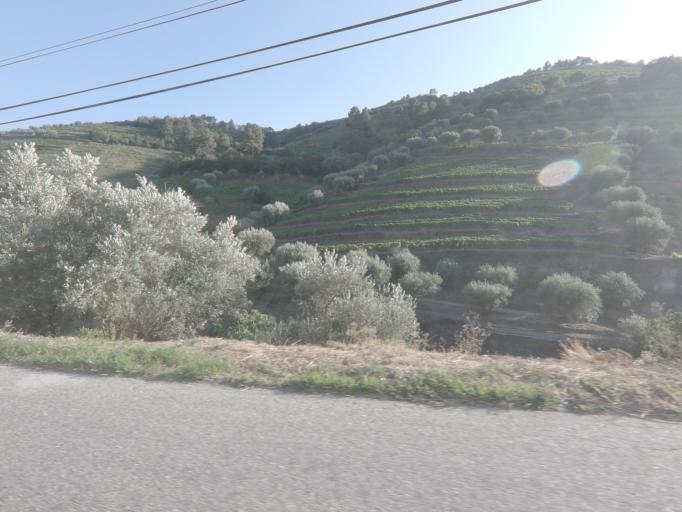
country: PT
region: Vila Real
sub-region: Sabrosa
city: Vilela
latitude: 41.1840
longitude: -7.5859
